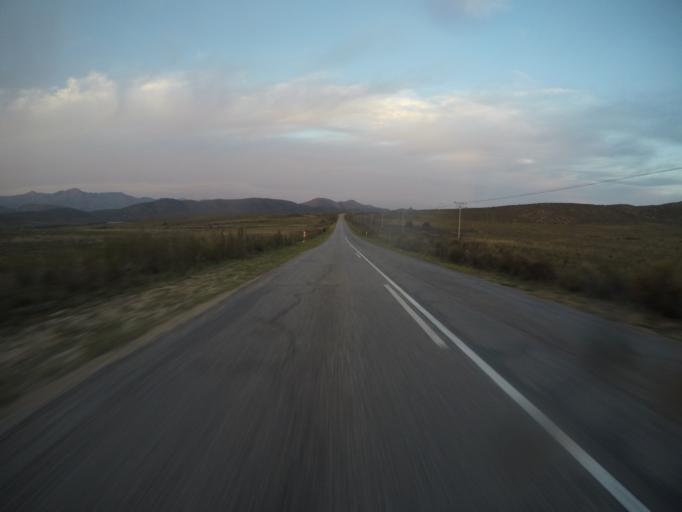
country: ZA
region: Western Cape
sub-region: Eden District Municipality
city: Plettenberg Bay
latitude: -33.7433
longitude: 23.4552
